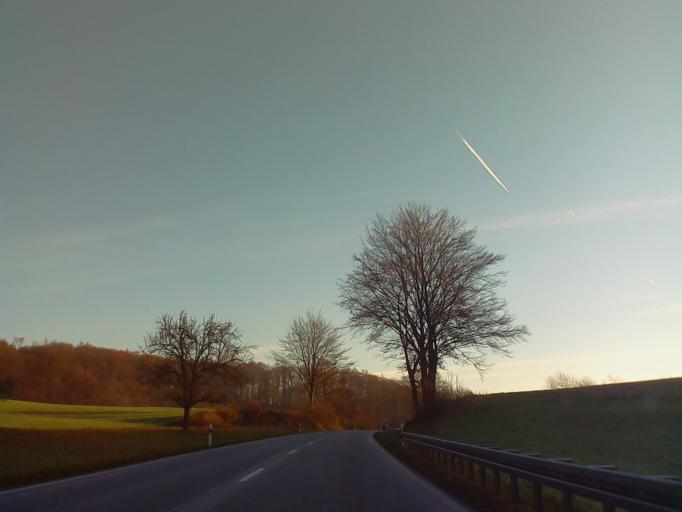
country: DE
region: Baden-Wuerttemberg
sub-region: Karlsruhe Region
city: Laudenbach
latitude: 49.6503
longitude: 8.7012
